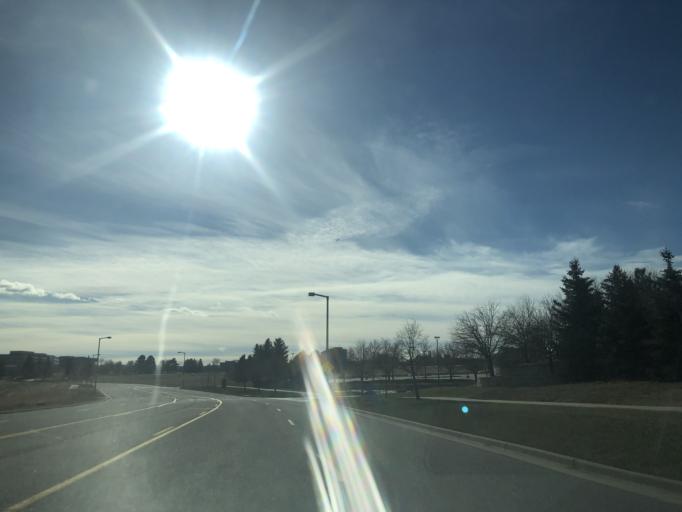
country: US
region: Colorado
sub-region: Douglas County
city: Meridian
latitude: 39.5488
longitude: -104.8659
